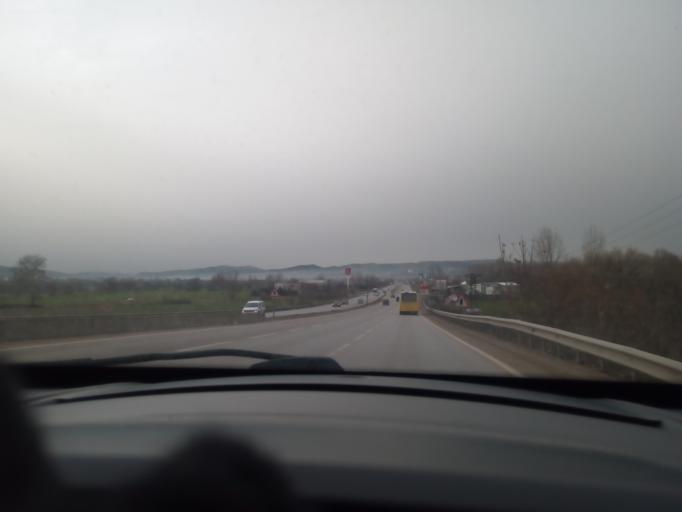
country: TR
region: Balikesir
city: Susurluk
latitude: 39.9431
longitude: 28.1658
